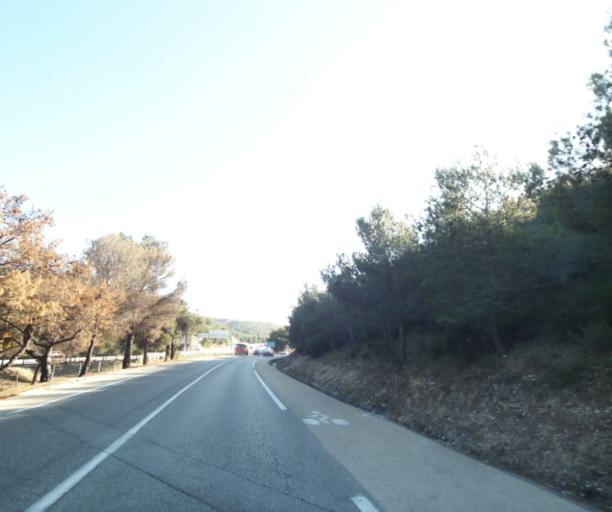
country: FR
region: Provence-Alpes-Cote d'Azur
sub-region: Departement des Bouches-du-Rhone
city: Roquefort-la-Bedoule
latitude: 43.2205
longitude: 5.5803
